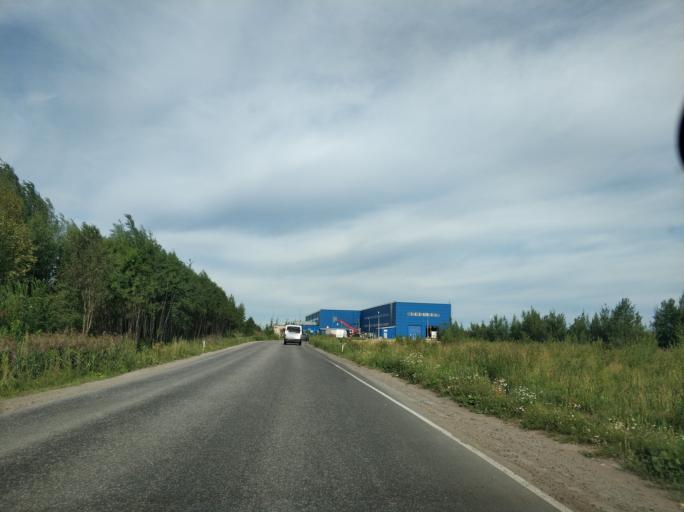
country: RU
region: St.-Petersburg
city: Grazhdanka
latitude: 60.0473
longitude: 30.4140
